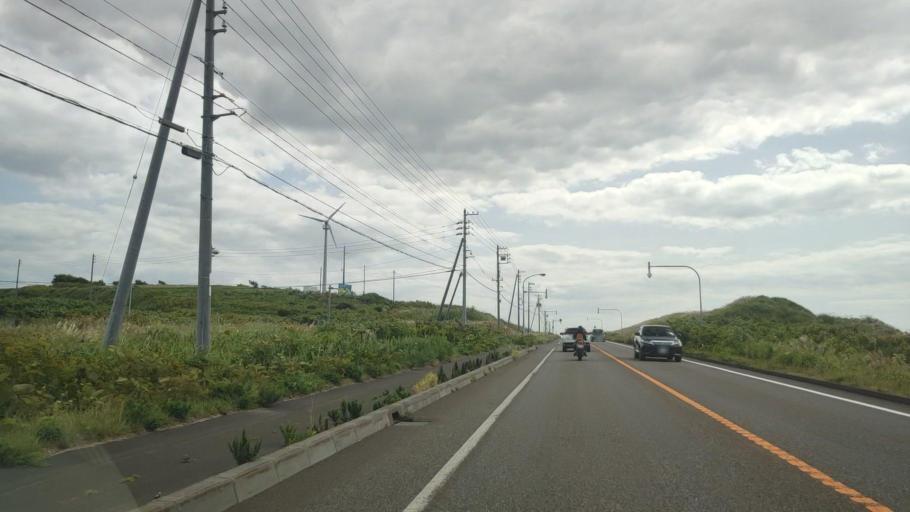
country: JP
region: Hokkaido
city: Rumoi
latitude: 44.5228
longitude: 141.7656
